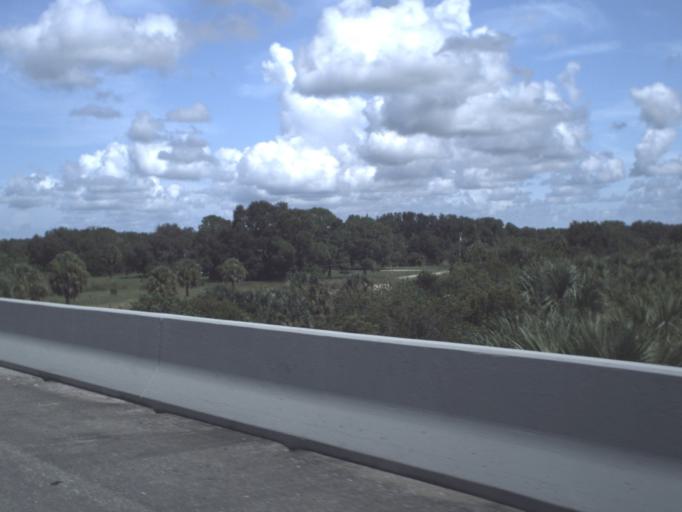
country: US
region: Florida
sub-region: Sarasota County
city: Laurel
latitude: 27.1560
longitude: -82.4232
